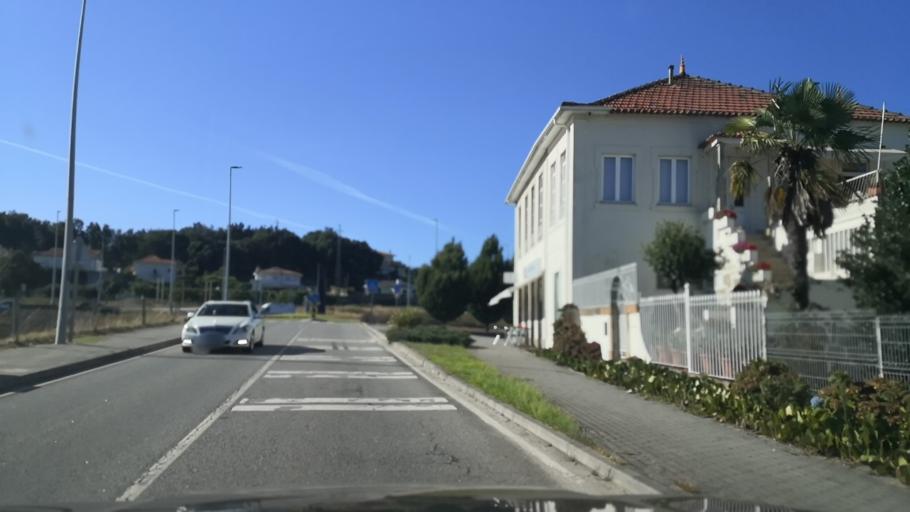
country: PT
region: Porto
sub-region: Santo Tirso
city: Santo Tirso
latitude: 41.3521
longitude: -8.4668
